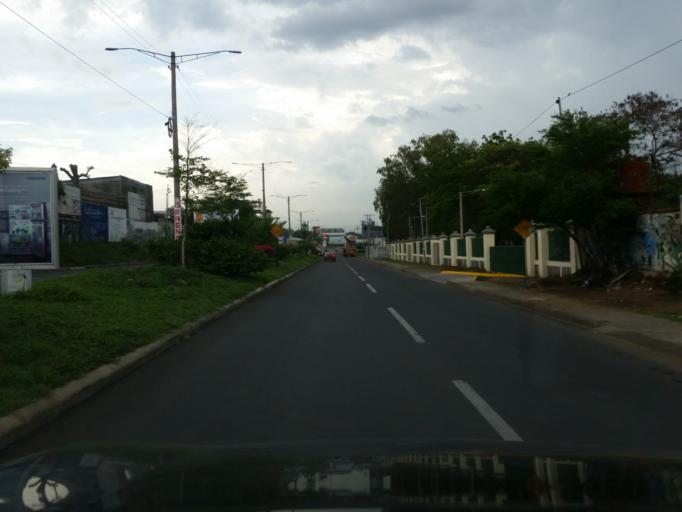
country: NI
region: Managua
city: Managua
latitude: 12.1248
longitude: -86.2593
